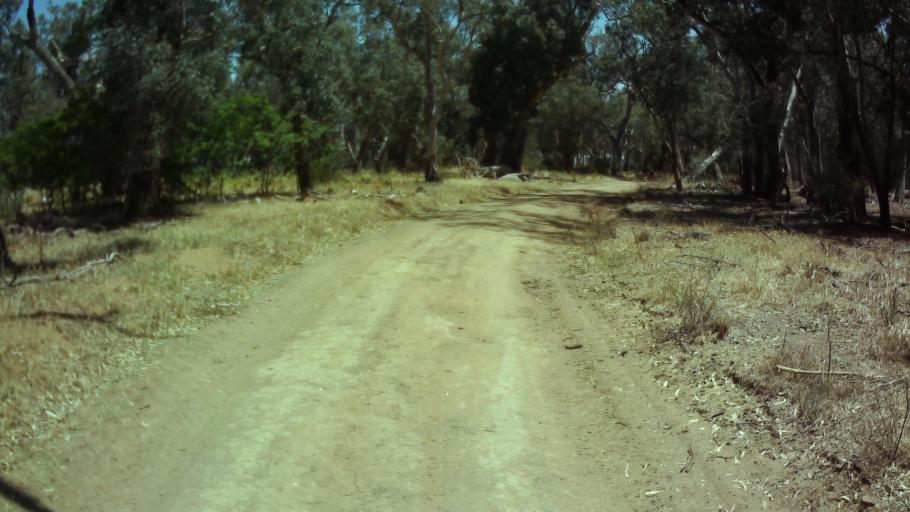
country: AU
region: New South Wales
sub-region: Weddin
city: Grenfell
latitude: -34.0460
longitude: 147.8368
